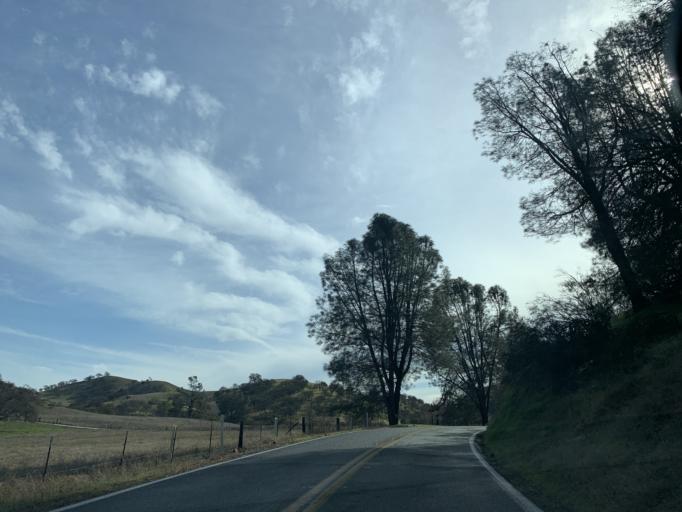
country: US
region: California
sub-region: Monterey County
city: Greenfield
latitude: 36.5074
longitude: -121.1105
